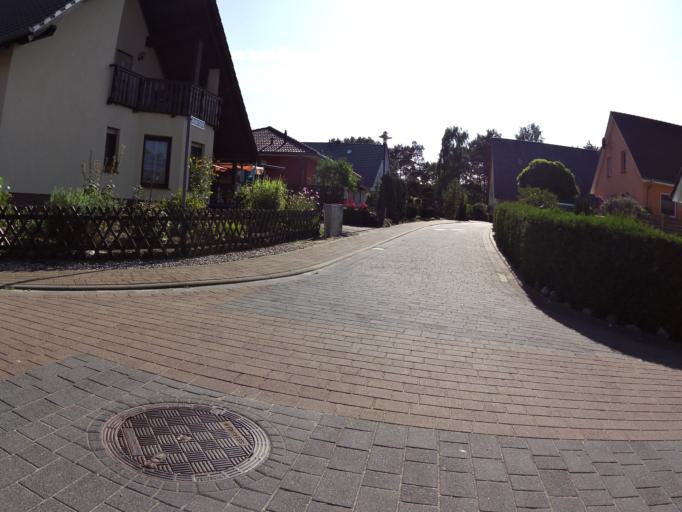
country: DE
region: Mecklenburg-Vorpommern
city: Seebad Heringsdorf
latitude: 53.9344
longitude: 14.1970
